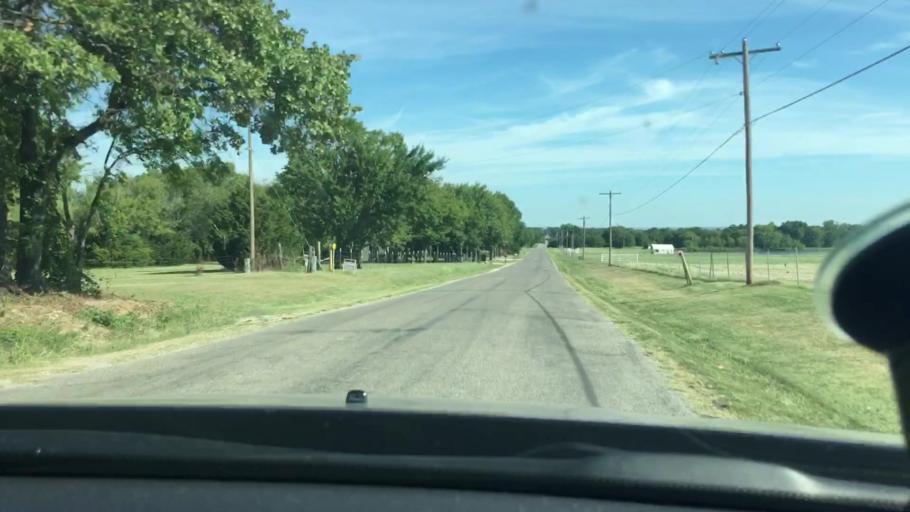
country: US
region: Oklahoma
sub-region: Carter County
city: Lone Grove
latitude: 34.2262
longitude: -97.2474
